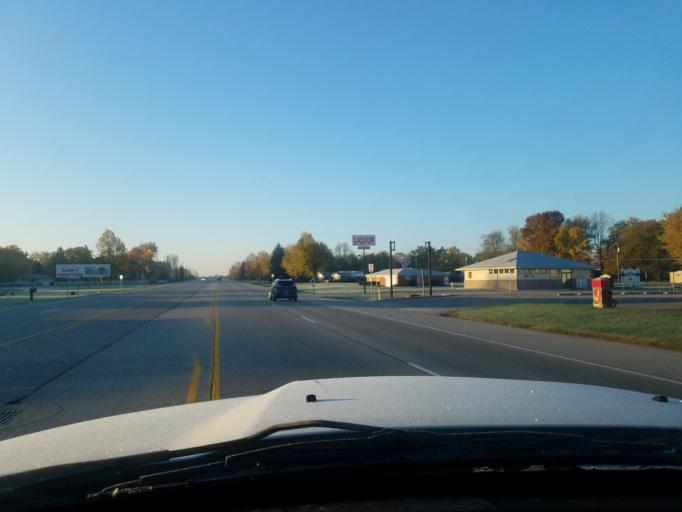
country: US
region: Indiana
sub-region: Montgomery County
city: Crawfordsville
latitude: 40.0741
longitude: -86.9060
